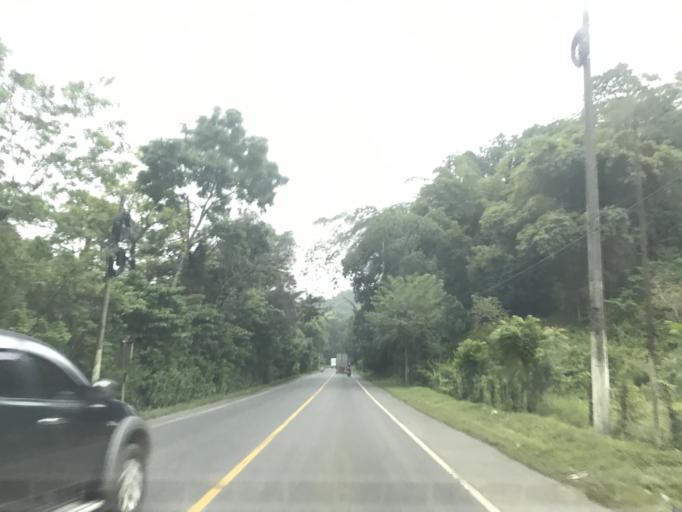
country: GT
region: Izabal
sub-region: Municipio de Puerto Barrios
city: Puerto Barrios
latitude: 15.6662
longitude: -88.5597
